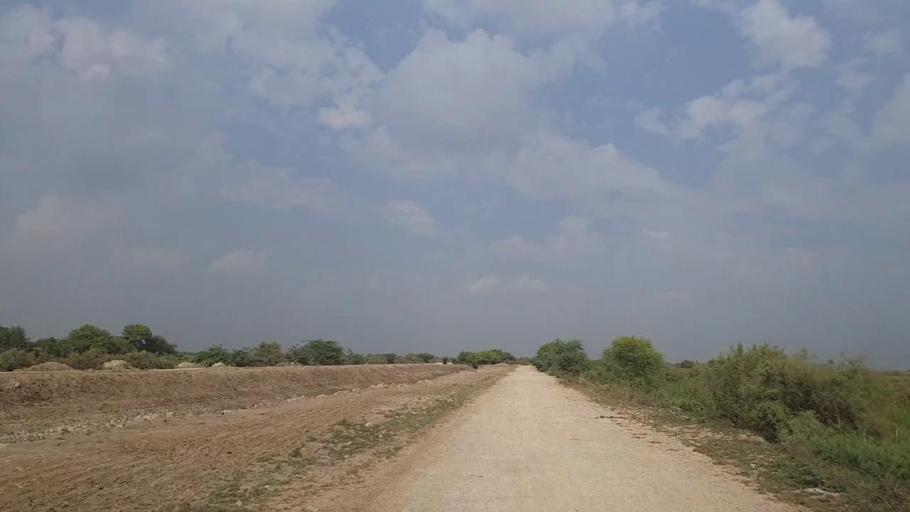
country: PK
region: Sindh
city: Daro Mehar
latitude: 24.6968
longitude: 68.1271
